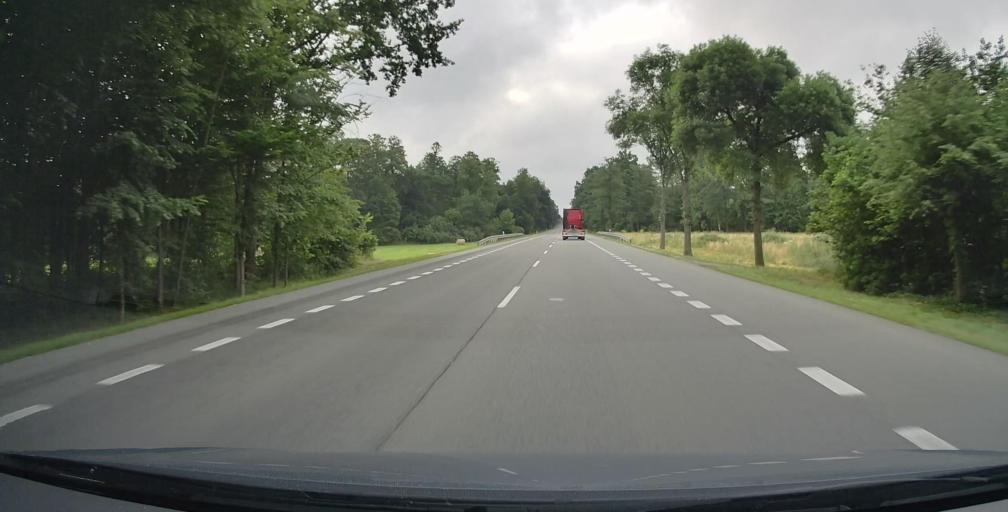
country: PL
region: Lublin Voivodeship
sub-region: Powiat lukowski
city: Trzebieszow
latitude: 52.0568
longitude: 22.6313
